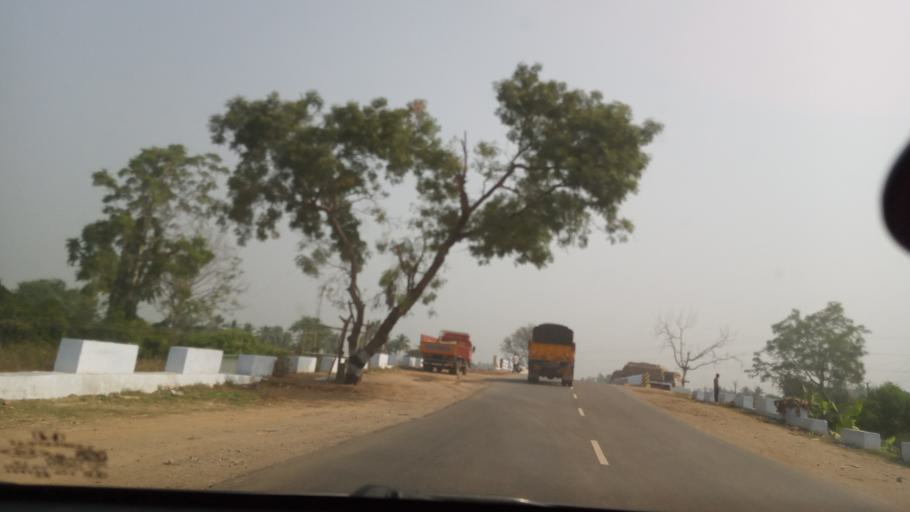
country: IN
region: Tamil Nadu
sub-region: Erode
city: Sathyamangalam
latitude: 11.4488
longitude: 77.2122
